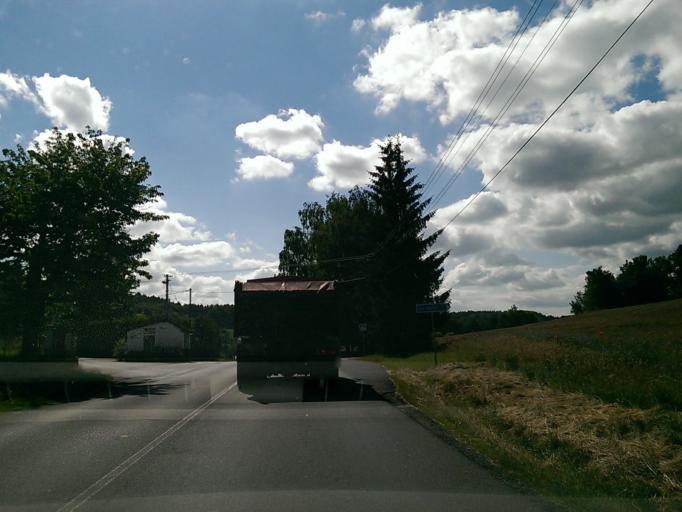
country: CZ
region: Liberecky
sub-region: Okres Semily
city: Turnov
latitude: 50.5850
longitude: 15.2088
